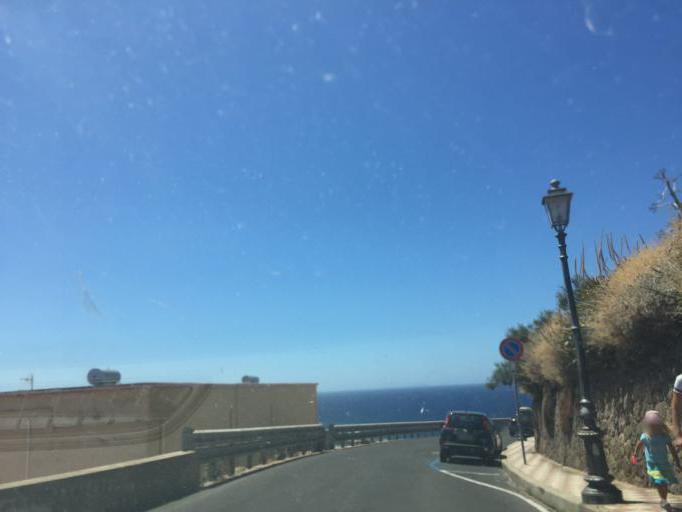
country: IT
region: Sardinia
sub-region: Provincia di Sassari
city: Castelsardo
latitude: 40.9150
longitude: 8.7126
